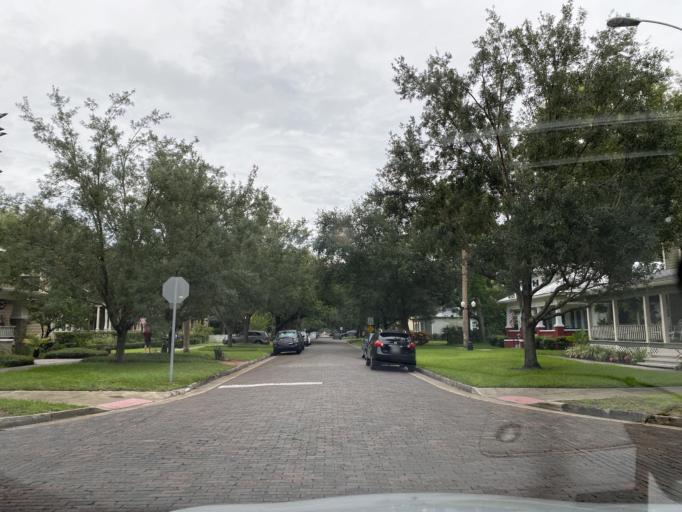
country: US
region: Florida
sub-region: Seminole County
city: Sanford
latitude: 28.8044
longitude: -81.2669
